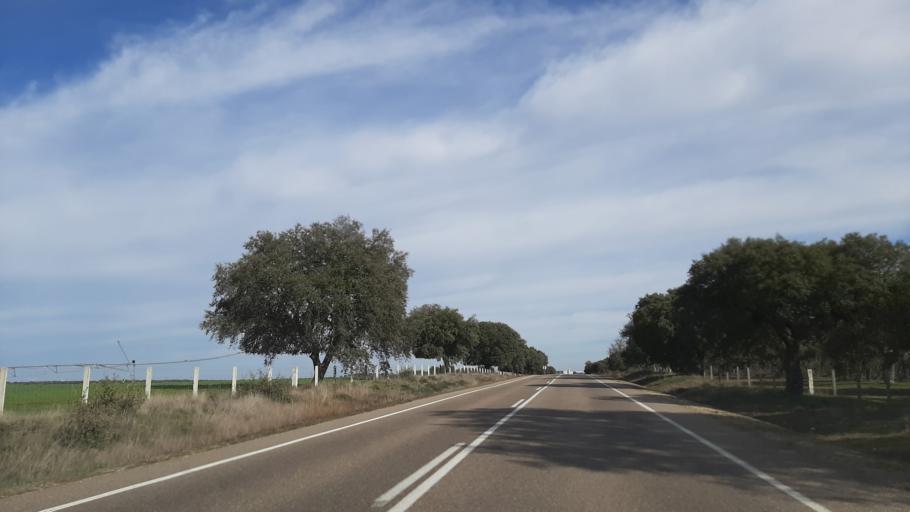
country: ES
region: Castille and Leon
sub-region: Provincia de Salamanca
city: Anover de Tormes
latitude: 41.0893
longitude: -5.9296
